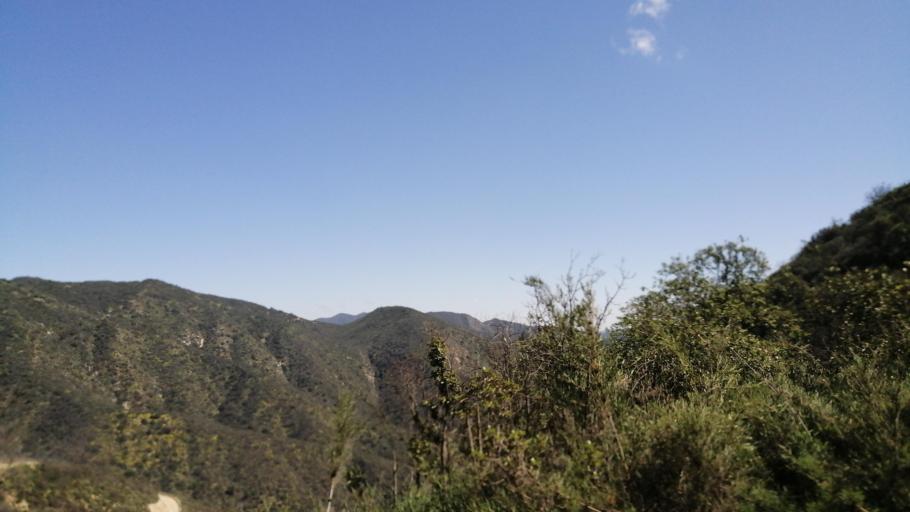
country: CL
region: Valparaiso
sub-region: Provincia de Marga Marga
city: Limache
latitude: -33.2044
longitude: -71.2545
